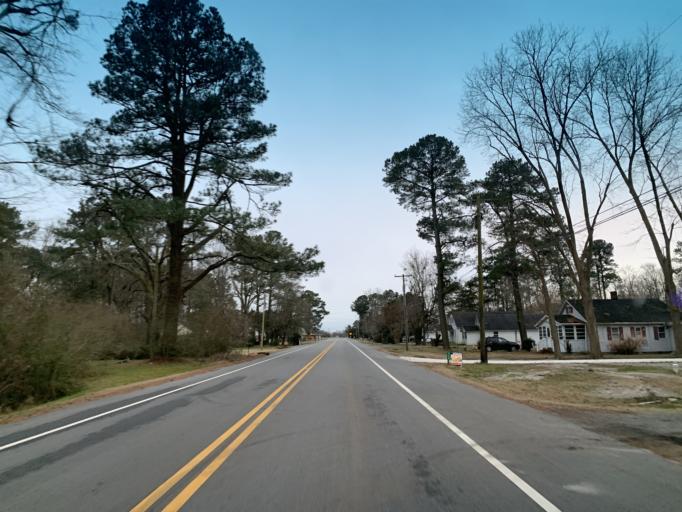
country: US
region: Maryland
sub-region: Worcester County
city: Pocomoke City
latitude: 38.0710
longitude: -75.5467
